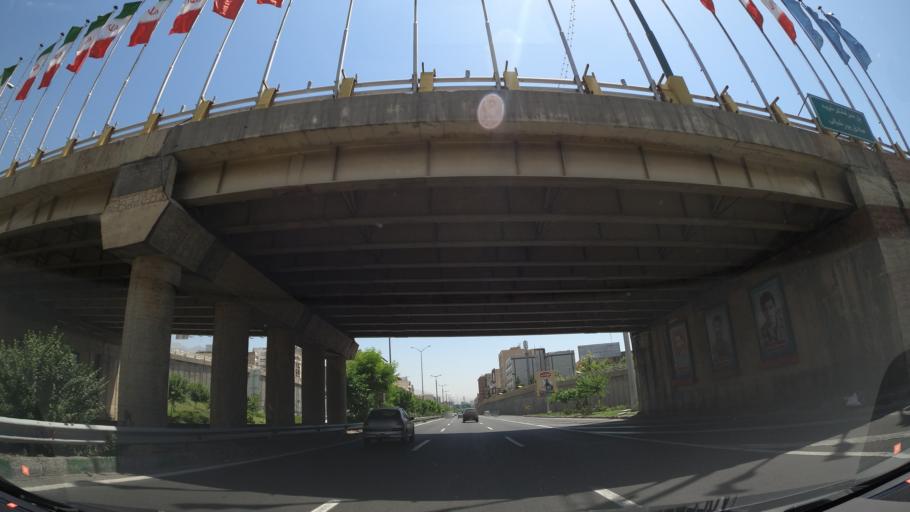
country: IR
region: Tehran
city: Tajrish
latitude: 35.7767
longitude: 51.3762
